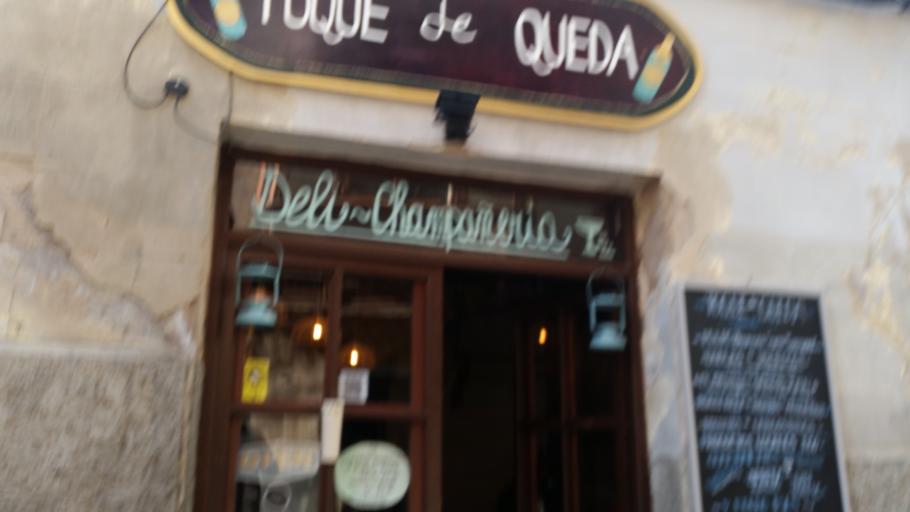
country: ES
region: Balearic Islands
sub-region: Illes Balears
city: Palma
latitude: 39.5733
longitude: 2.6472
